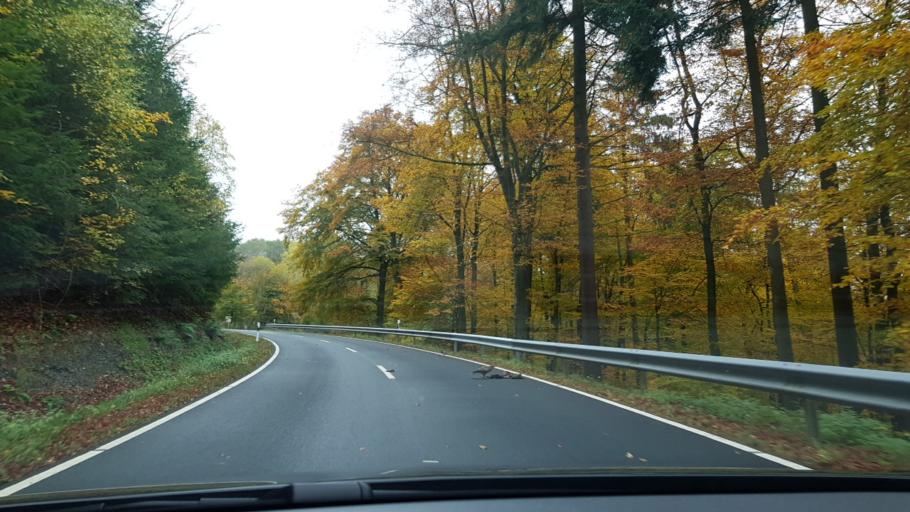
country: DE
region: Rheinland-Pfalz
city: Polich
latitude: 49.7821
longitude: 6.8497
